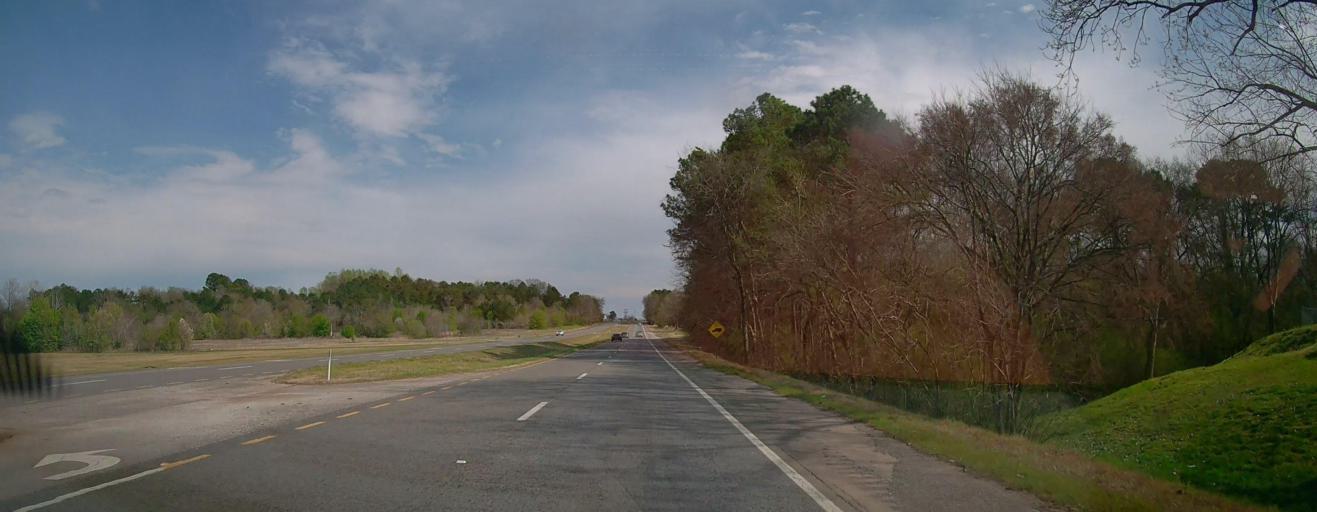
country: US
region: Alabama
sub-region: Jefferson County
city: Adamsville
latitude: 33.6034
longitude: -86.9522
